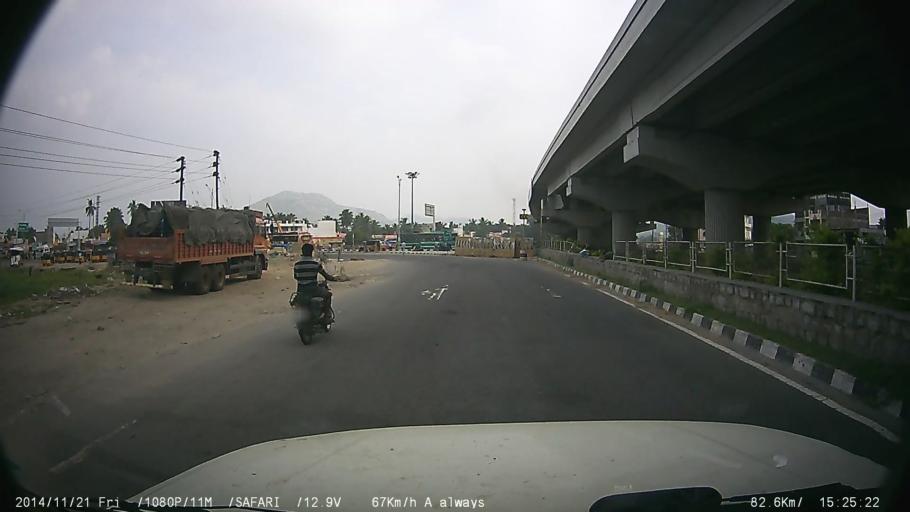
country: IN
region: Tamil Nadu
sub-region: Krishnagiri
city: Krishnagiri
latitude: 12.5078
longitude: 78.2223
